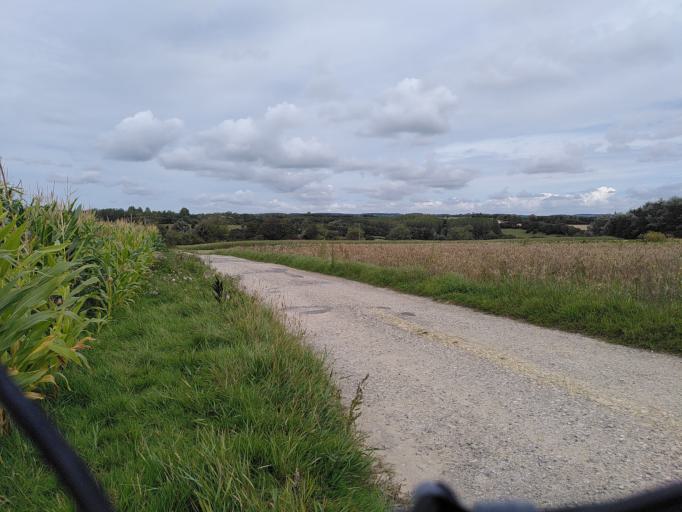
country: FR
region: Nord-Pas-de-Calais
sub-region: Departement du Pas-de-Calais
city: Longfosse
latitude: 50.7048
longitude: 1.7659
